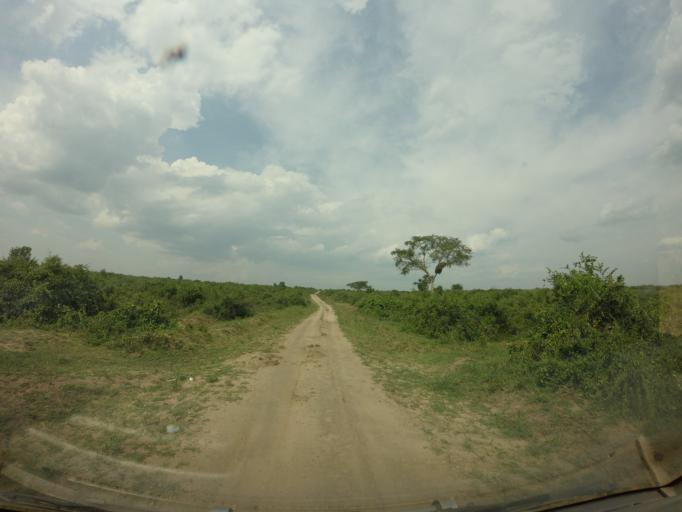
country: UG
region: Western Region
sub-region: Rubirizi District
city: Rubirizi
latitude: -0.2100
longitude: 29.9131
